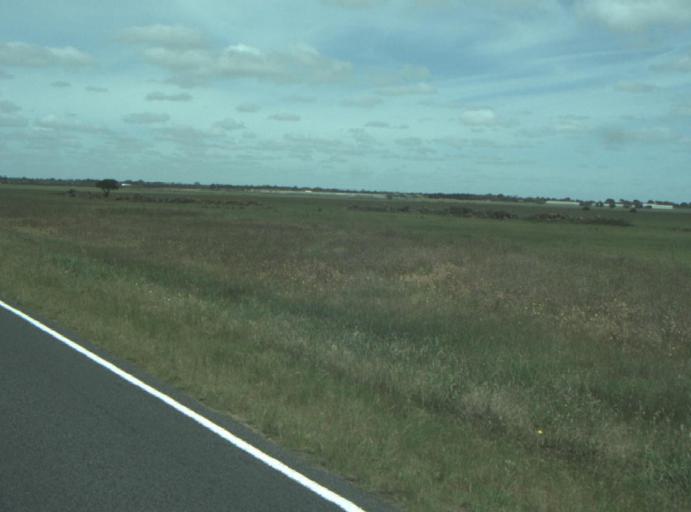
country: AU
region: Victoria
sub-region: Wyndham
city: Little River
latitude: -38.0047
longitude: 144.4668
